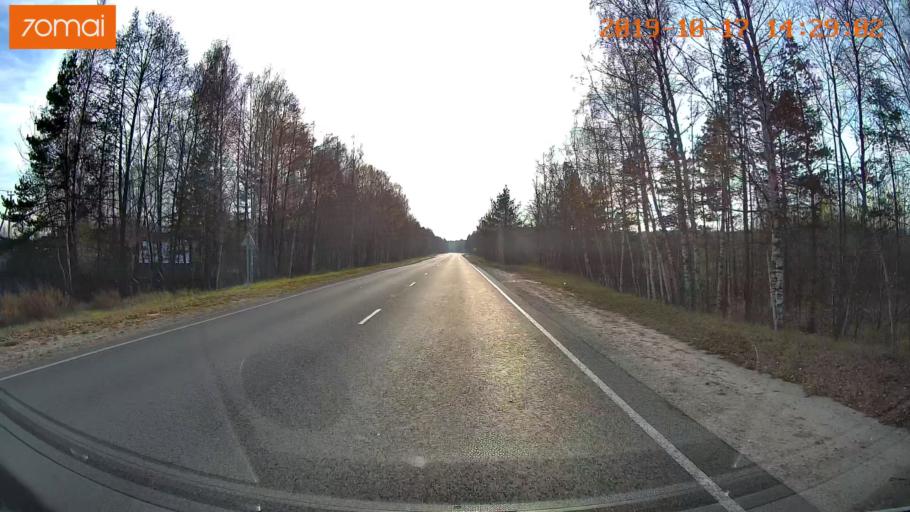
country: RU
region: Rjazan
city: Solotcha
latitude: 54.9657
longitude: 39.9470
